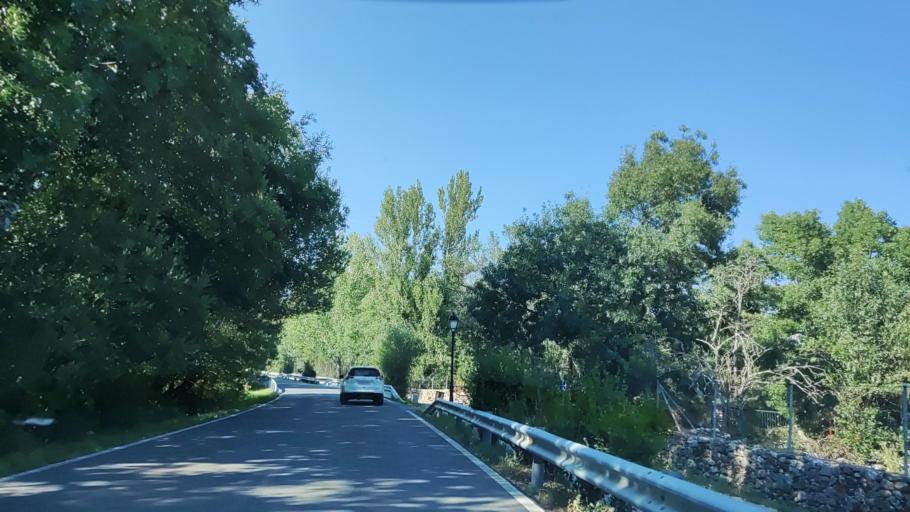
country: ES
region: Madrid
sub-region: Provincia de Madrid
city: Rascafria
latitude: 40.8954
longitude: -3.8803
